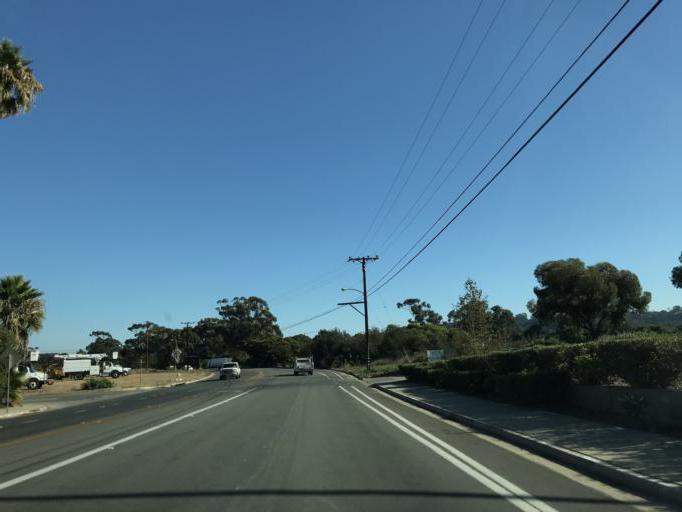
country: US
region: California
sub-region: Santa Barbara County
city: Goleta
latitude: 34.4432
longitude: -119.7876
